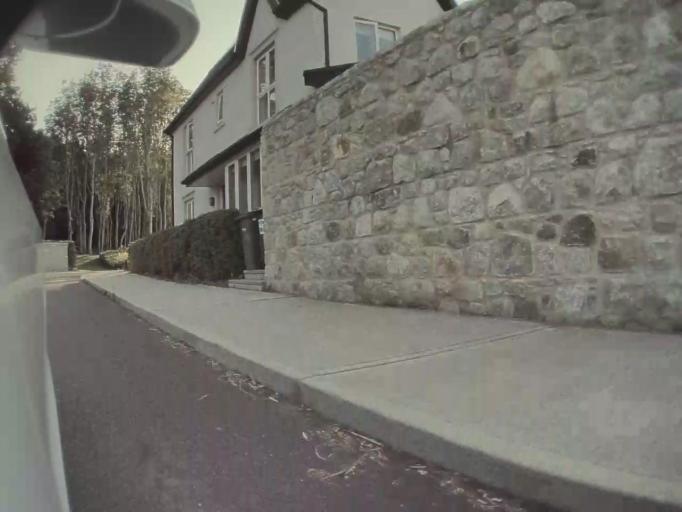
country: IE
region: Leinster
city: Foxrock
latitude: 53.2404
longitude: -6.2005
